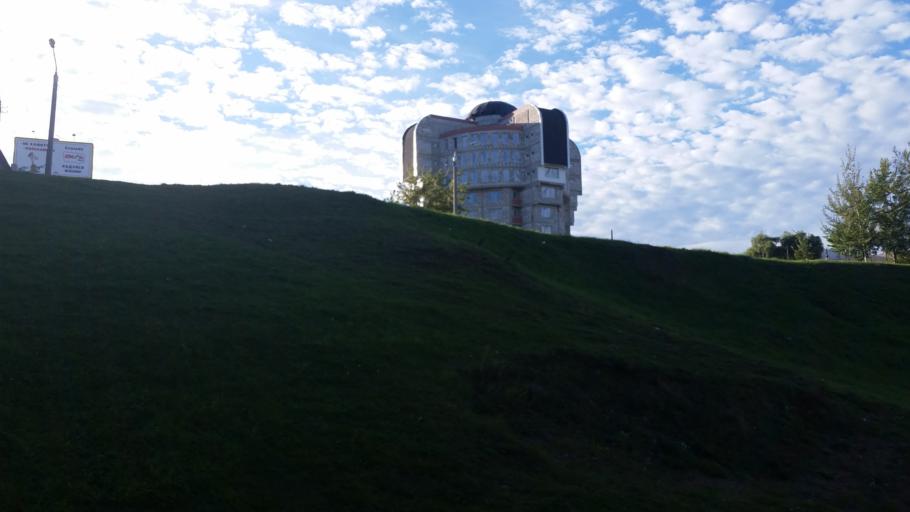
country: BY
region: Vitebsk
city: Vitebsk
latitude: 55.1844
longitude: 30.1968
